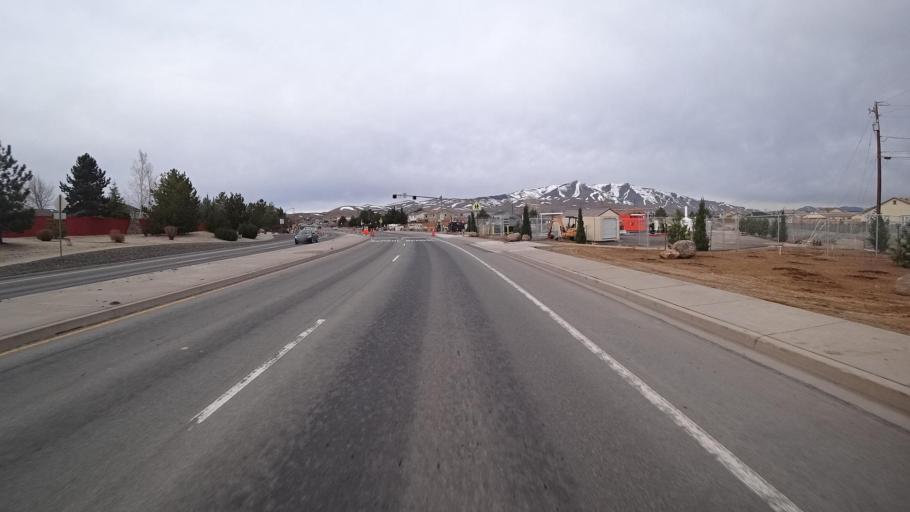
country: US
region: Nevada
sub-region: Washoe County
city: Golden Valley
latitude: 39.6073
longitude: -119.8333
